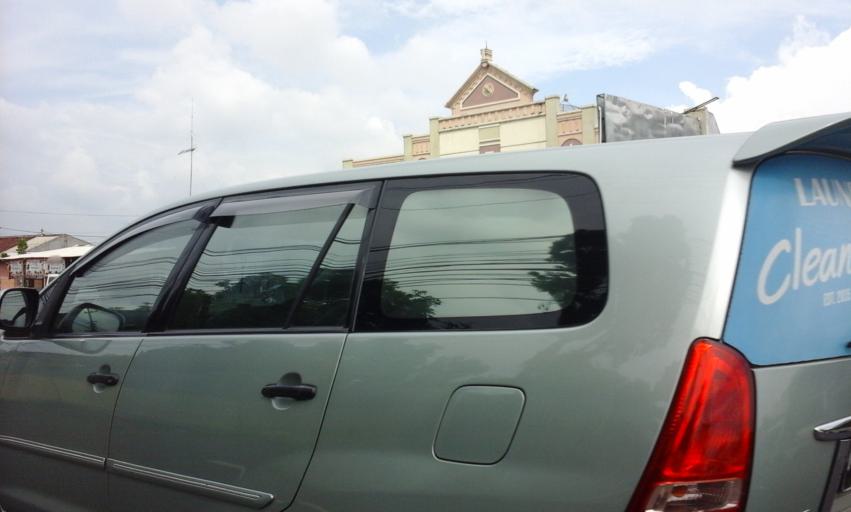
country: ID
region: East Java
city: Krajan
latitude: -8.1850
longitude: 113.6651
